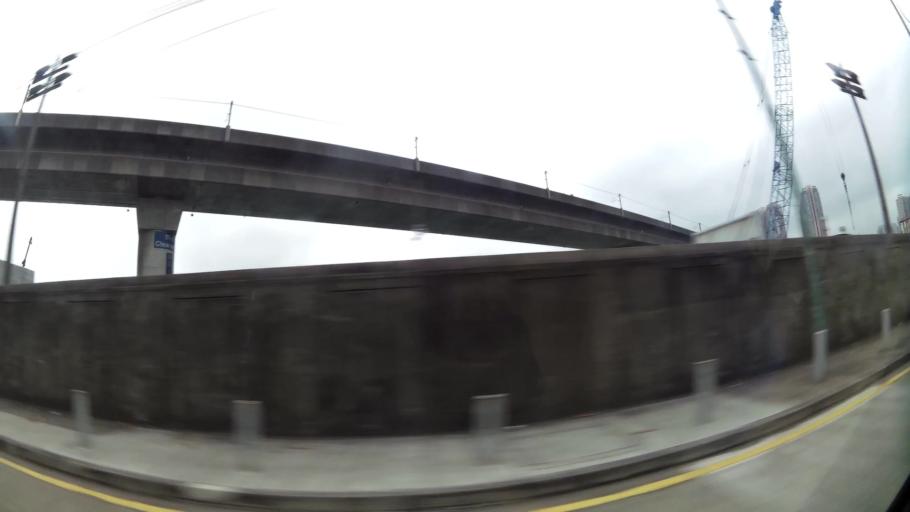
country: HK
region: Tsuen Wan
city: Tsuen Wan
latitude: 22.3565
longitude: 114.1154
